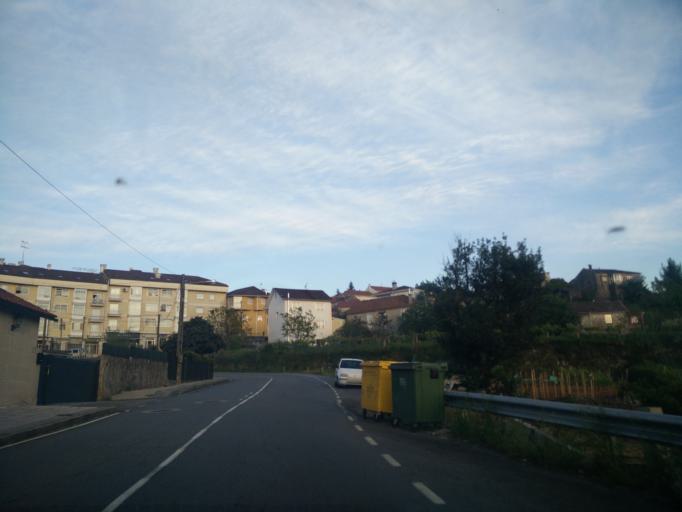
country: ES
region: Galicia
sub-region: Provincia de Pontevedra
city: Mondariz
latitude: 42.2330
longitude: -8.4591
